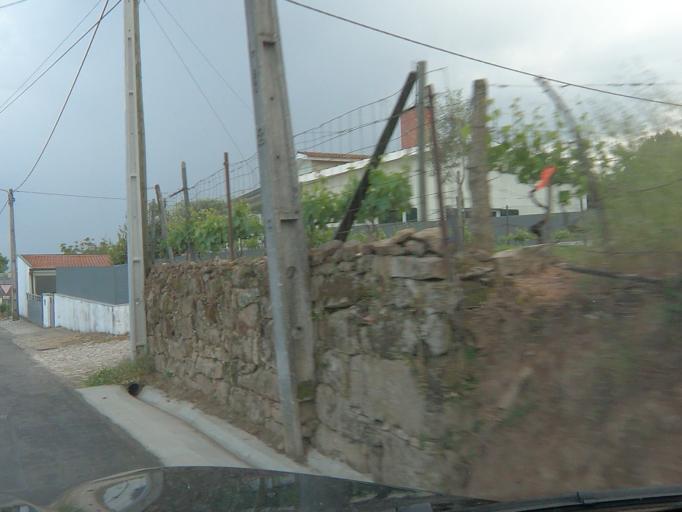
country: PT
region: Vila Real
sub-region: Vila Real
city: Vila Real
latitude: 41.3467
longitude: -7.7233
